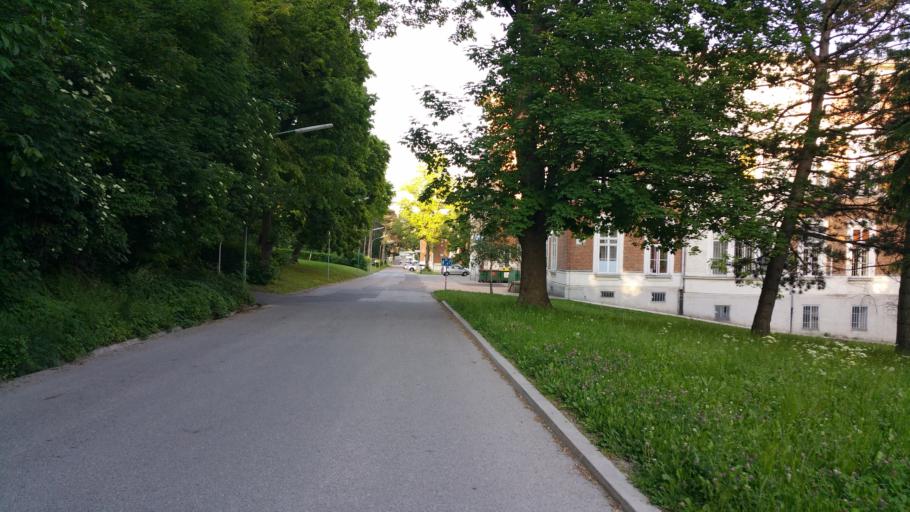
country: AT
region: Lower Austria
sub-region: Politischer Bezirk Modling
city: Perchtoldsdorf
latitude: 48.2087
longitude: 16.2746
